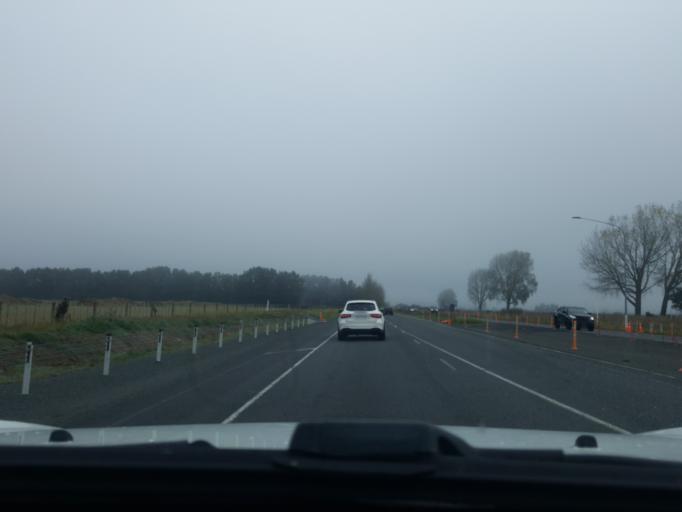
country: NZ
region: Waikato
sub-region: Waikato District
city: Te Kauwhata
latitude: -37.5011
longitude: 175.1643
